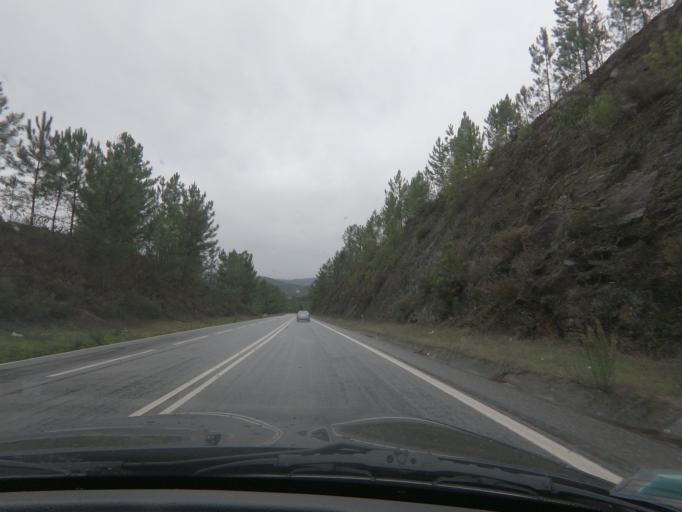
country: PT
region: Porto
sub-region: Amarante
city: Amarante
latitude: 41.3234
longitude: -8.0538
